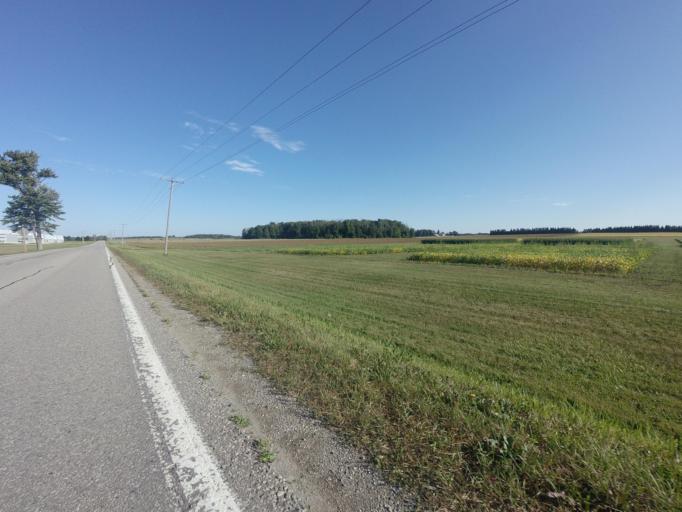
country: CA
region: Ontario
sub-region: Wellington County
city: Guelph
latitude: 43.6436
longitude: -80.4061
